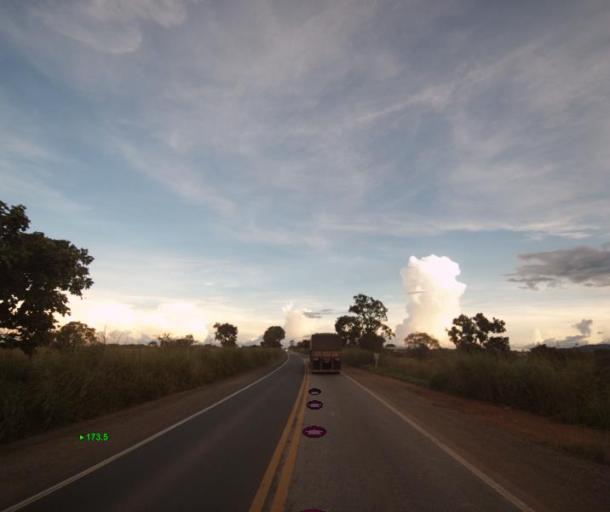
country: BR
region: Goias
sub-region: Uruacu
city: Uruacu
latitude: -14.2915
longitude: -49.1504
